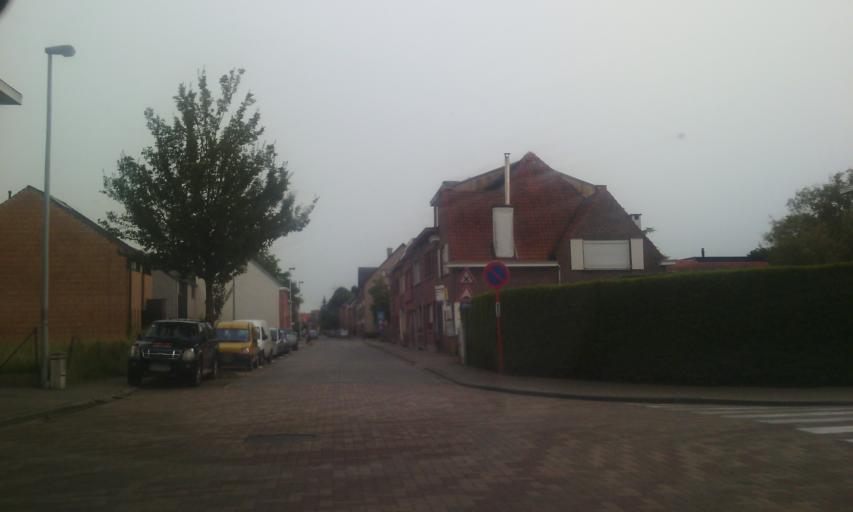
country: BE
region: Flanders
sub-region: Provincie Oost-Vlaanderen
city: Aalst
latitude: 50.9651
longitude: 4.0303
